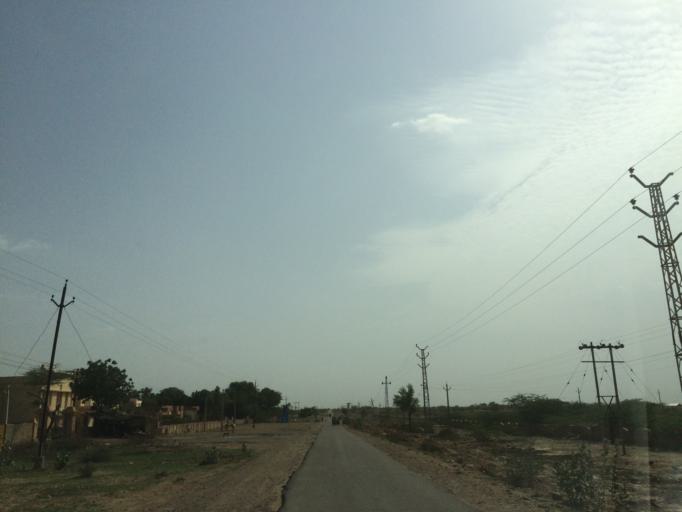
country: IN
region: Rajasthan
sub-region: Jaisalmer
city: Jaisalmer
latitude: 26.9029
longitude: 70.9321
